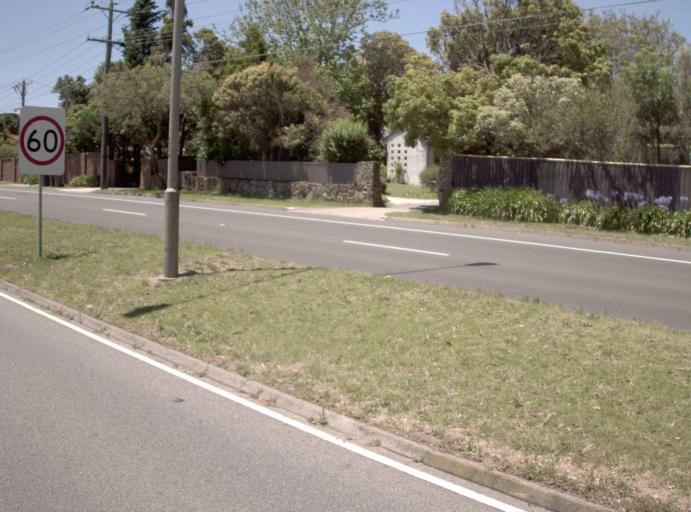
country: AU
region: Victoria
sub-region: Frankston
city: Frankston
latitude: -38.1608
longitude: 145.1036
